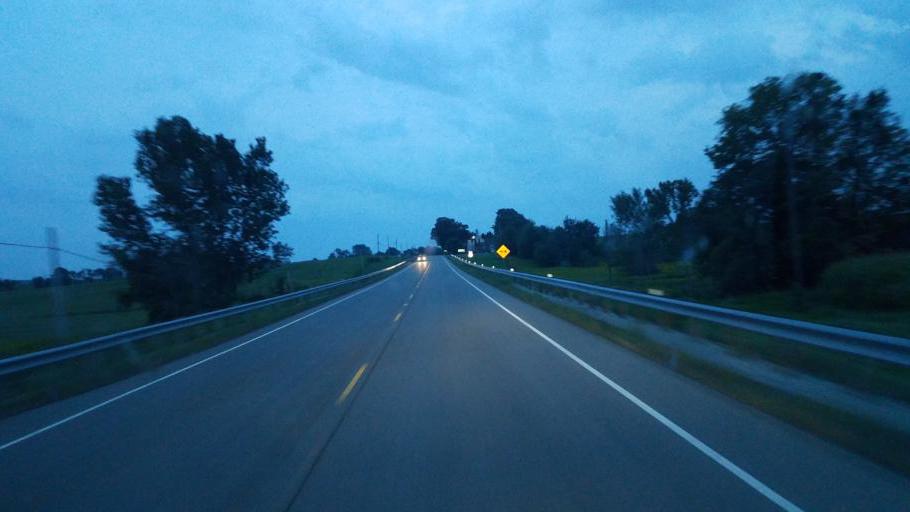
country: US
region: Ohio
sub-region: Knox County
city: Fredericktown
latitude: 40.5260
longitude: -82.5470
